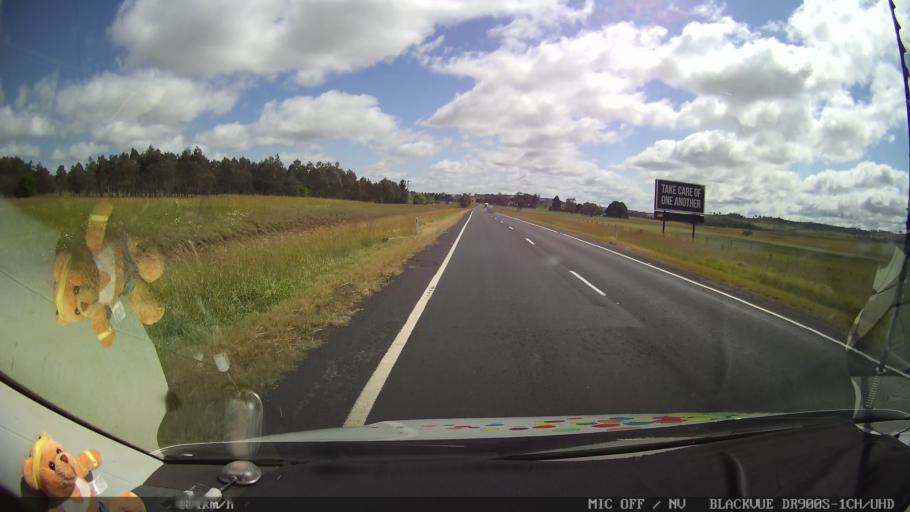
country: AU
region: New South Wales
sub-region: Glen Innes Severn
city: Glen Innes
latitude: -29.9160
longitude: 151.7281
